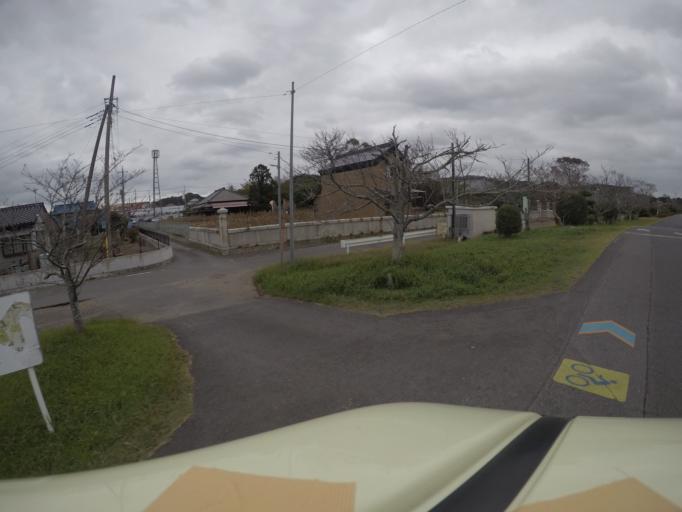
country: JP
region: Ibaraki
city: Itako
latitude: 35.9793
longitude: 140.4963
